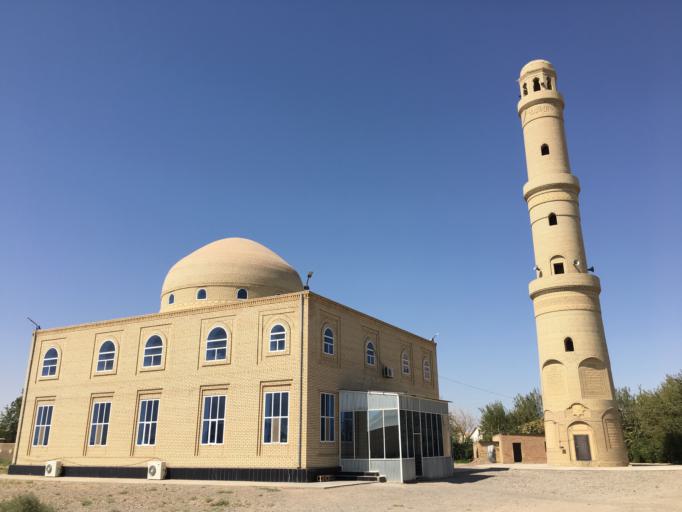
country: IR
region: Razavi Khorasan
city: Sarakhs
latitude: 36.5253
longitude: 61.2097
